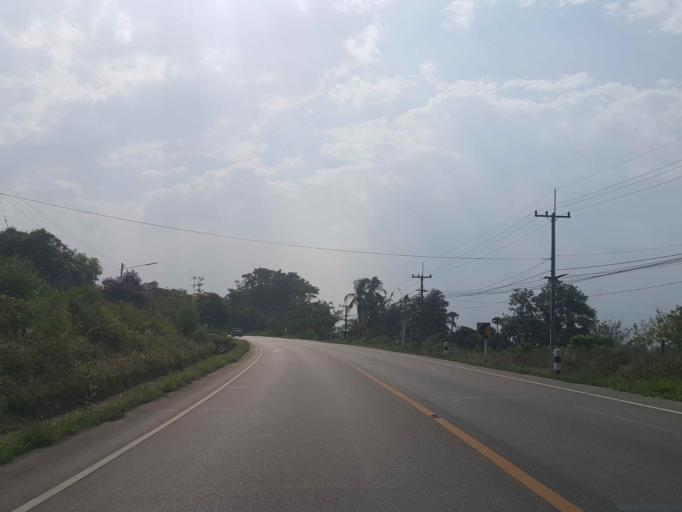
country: TH
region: Chiang Mai
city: Mae Taeng
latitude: 19.1070
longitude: 99.0451
